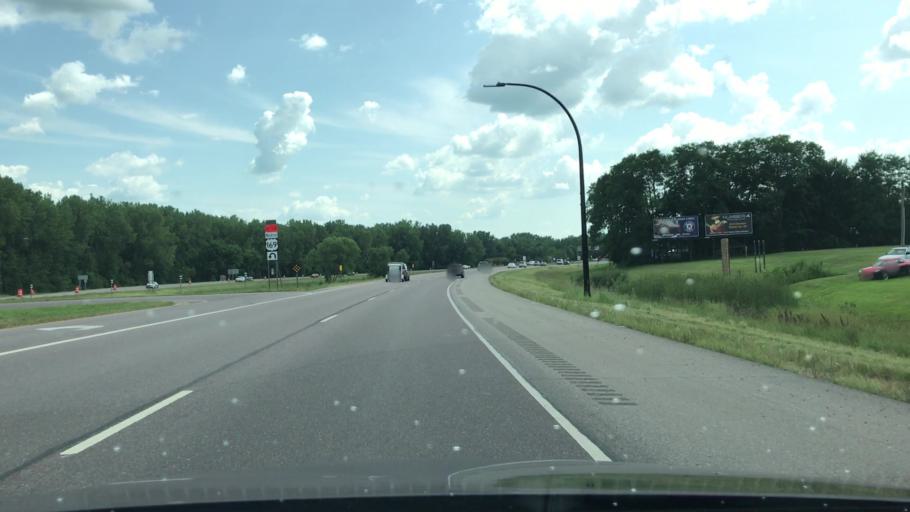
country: US
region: Minnesota
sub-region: Nicollet County
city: Saint Peter
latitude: 44.3384
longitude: -93.9482
